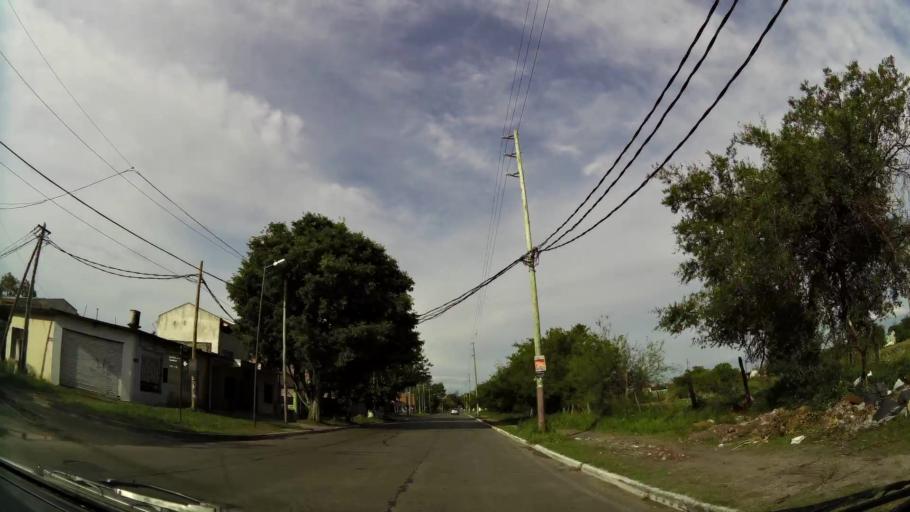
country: AR
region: Buenos Aires
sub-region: Partido de Quilmes
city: Quilmes
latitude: -34.7466
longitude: -58.2678
